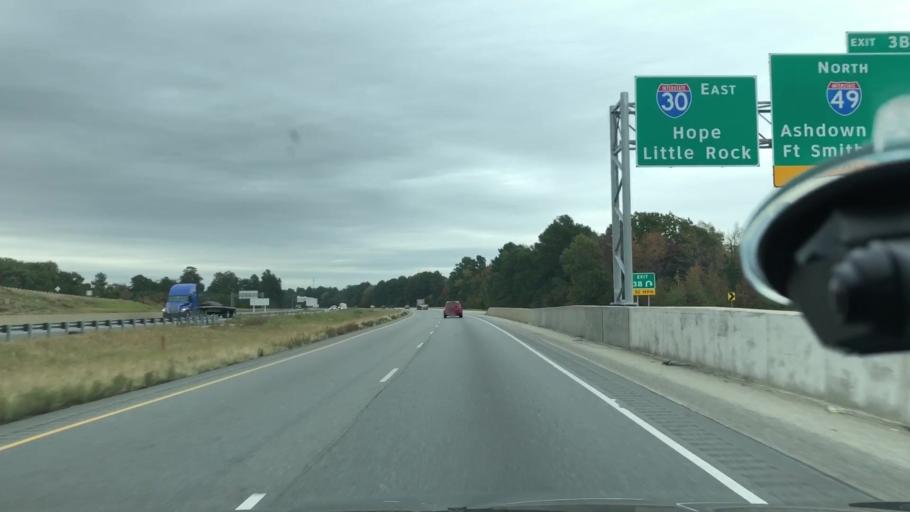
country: US
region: Arkansas
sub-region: Miller County
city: Texarkana
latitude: 33.4800
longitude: -93.9868
